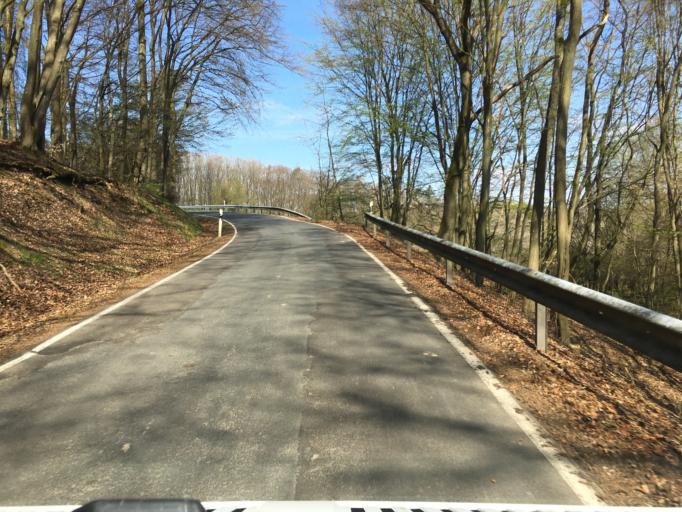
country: DE
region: Rheinland-Pfalz
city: Kirchsahr
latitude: 50.5122
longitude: 6.8998
